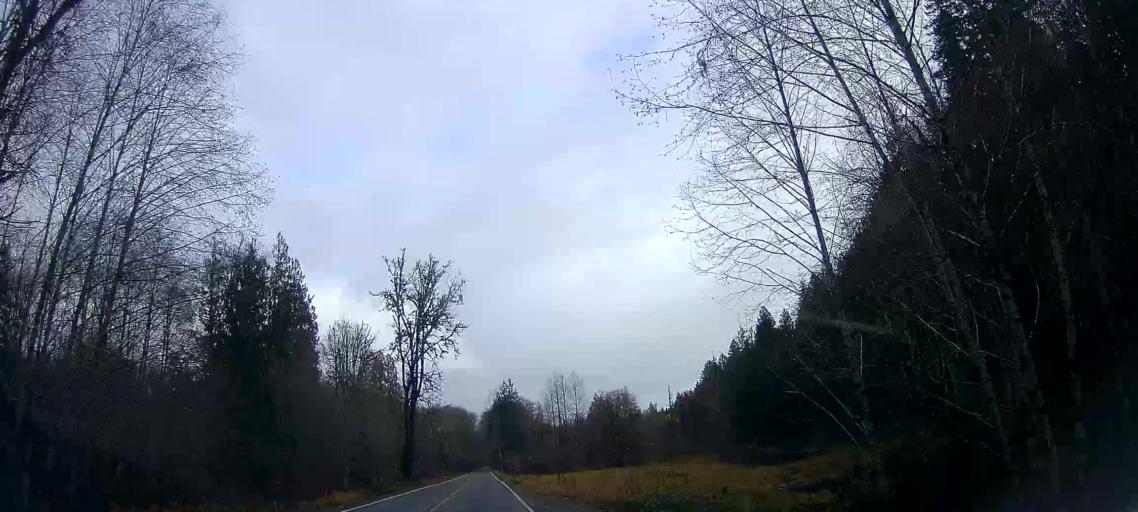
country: US
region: Washington
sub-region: Skagit County
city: Sedro-Woolley
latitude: 48.5126
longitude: -121.8807
